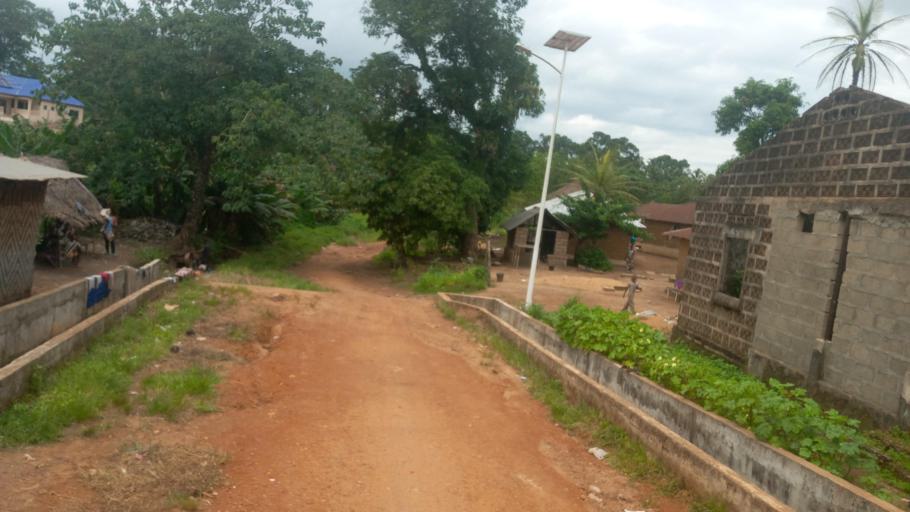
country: SL
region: Southern Province
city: Mogbwemo
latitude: 7.6056
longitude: -12.1753
